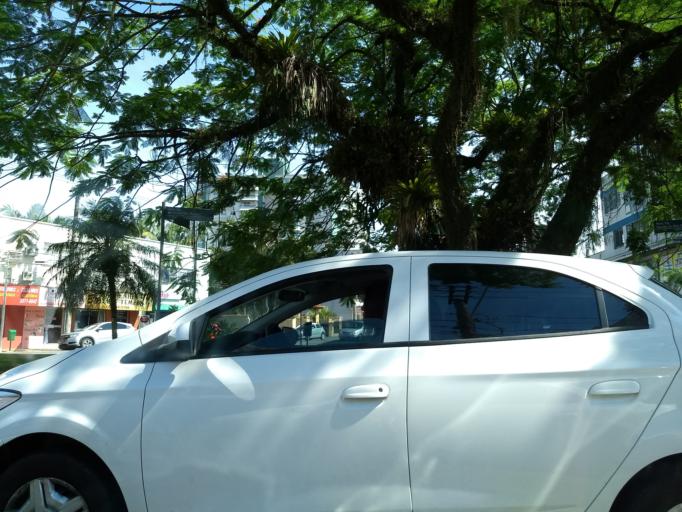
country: BR
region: Santa Catarina
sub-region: Jaragua Do Sul
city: Jaragua do Sul
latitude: -26.4913
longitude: -49.0830
